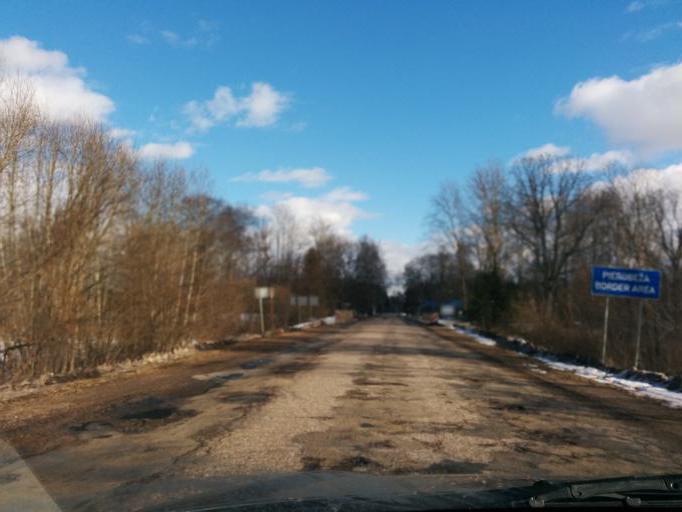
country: LV
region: Balvu Rajons
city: Balvi
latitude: 57.1782
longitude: 27.0995
